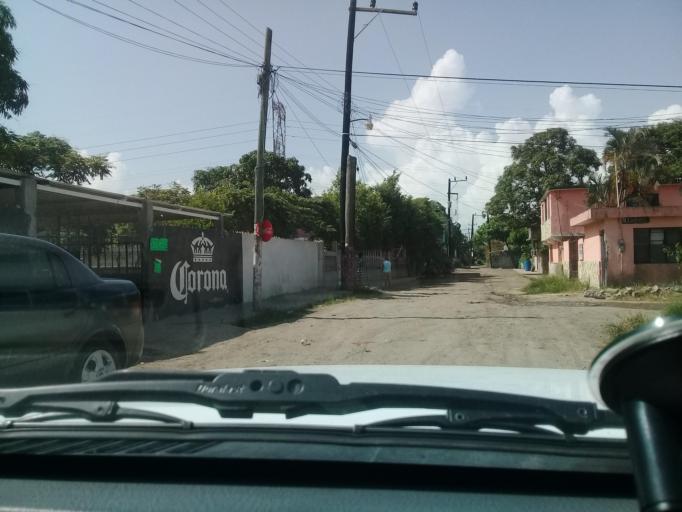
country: MX
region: Veracruz
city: Moralillo
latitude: 22.2276
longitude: -97.9032
